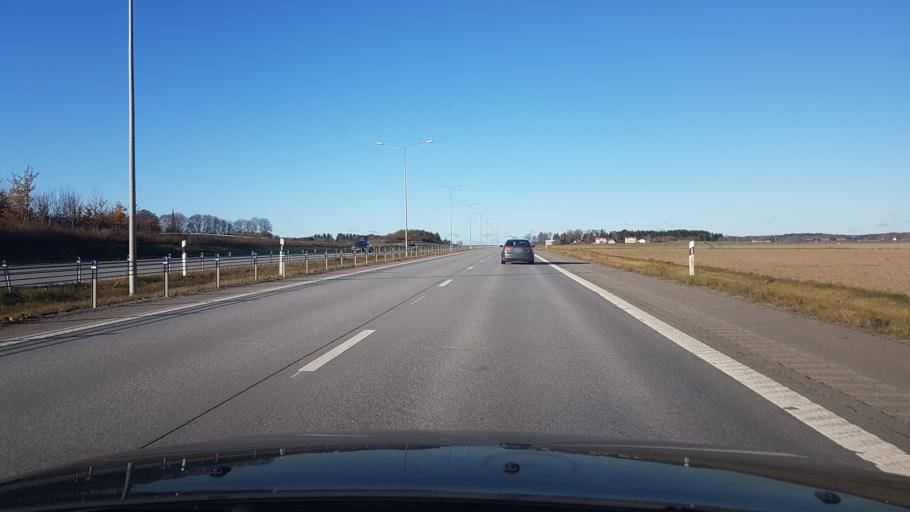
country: SE
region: Uppsala
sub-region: Uppsala Kommun
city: Saevja
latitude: 59.8716
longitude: 17.7030
